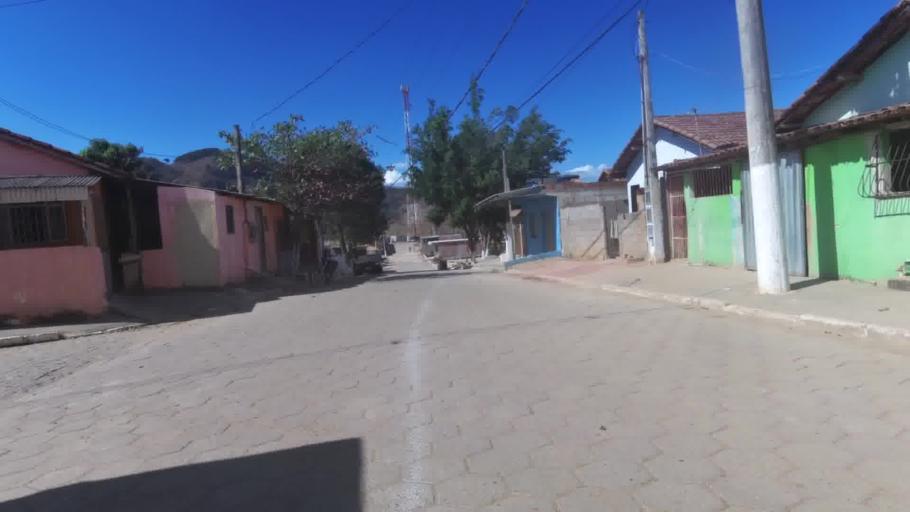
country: BR
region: Espirito Santo
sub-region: Cachoeiro De Itapemirim
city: Cachoeiro de Itapemirim
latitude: -20.9201
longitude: -41.1954
